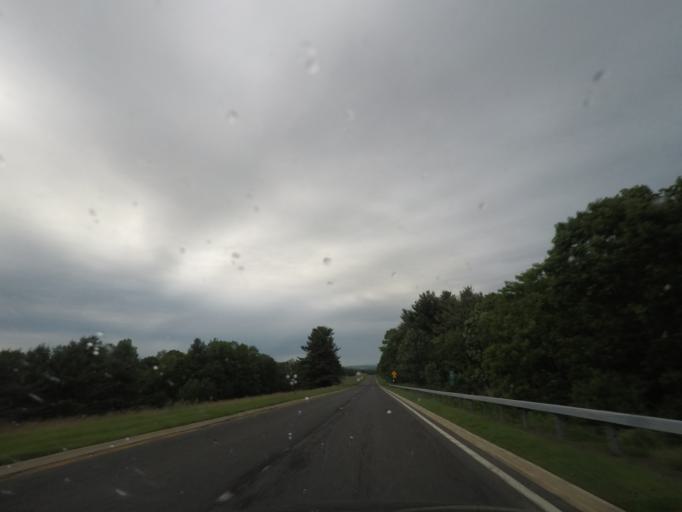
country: US
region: New York
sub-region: Columbia County
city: Chatham
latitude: 42.3151
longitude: -73.5771
